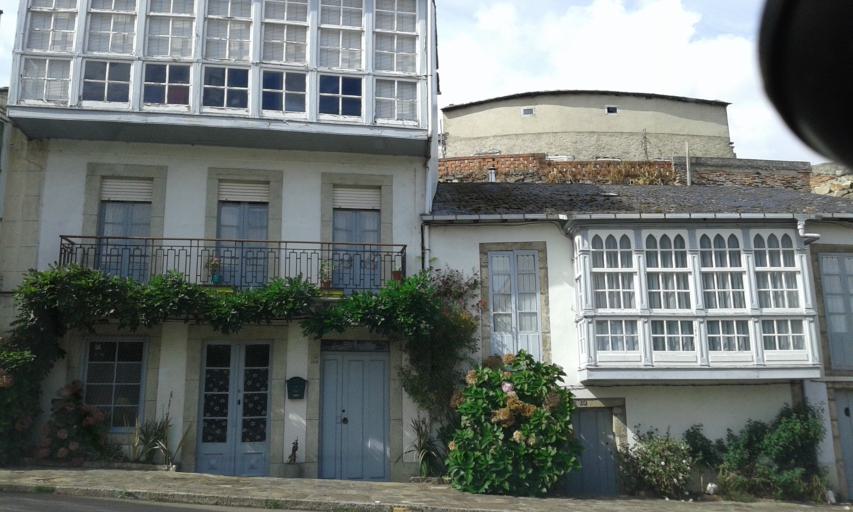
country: ES
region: Galicia
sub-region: Provincia de Ourense
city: Manzaneda
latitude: 42.3103
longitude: -7.2339
